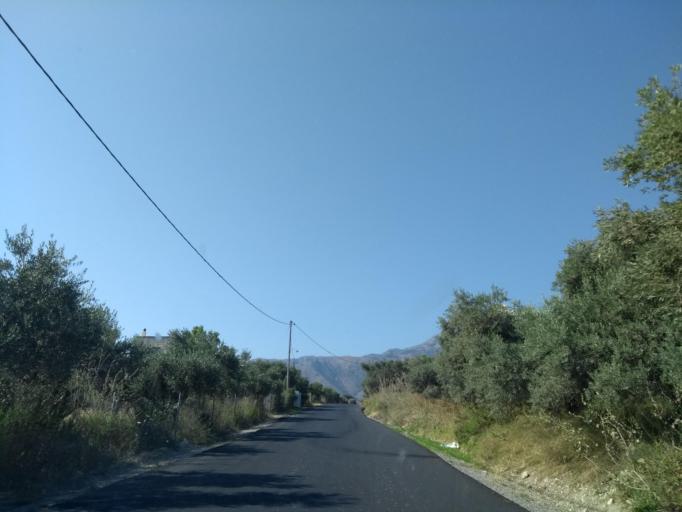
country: GR
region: Crete
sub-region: Nomos Chanias
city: Georgioupolis
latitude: 35.3363
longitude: 24.3019
